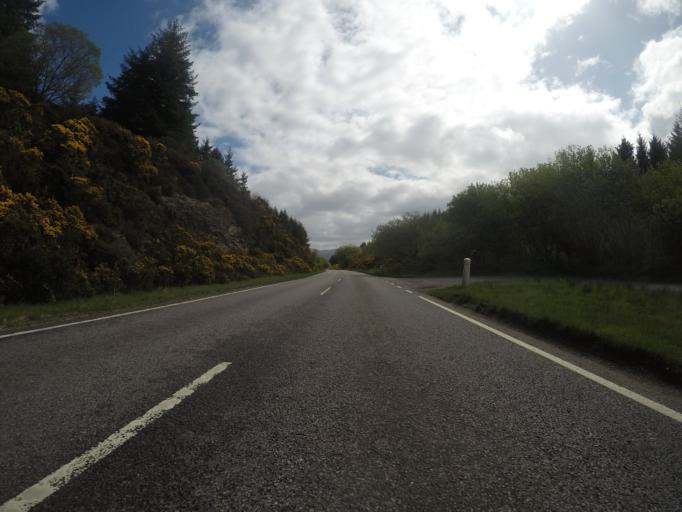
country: GB
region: Scotland
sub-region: Highland
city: Portree
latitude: 57.2456
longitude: -5.9254
